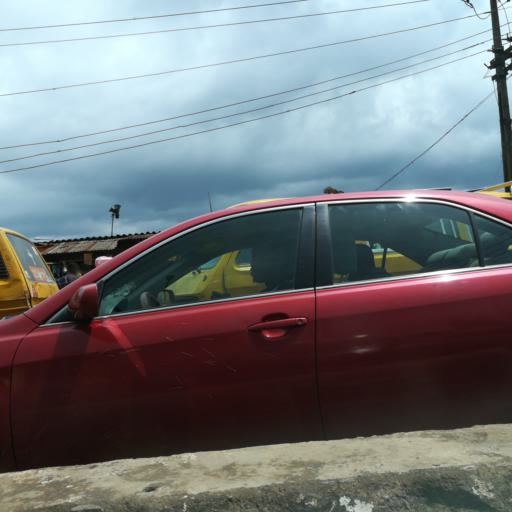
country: NG
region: Lagos
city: Agege
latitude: 6.5993
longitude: 3.2918
